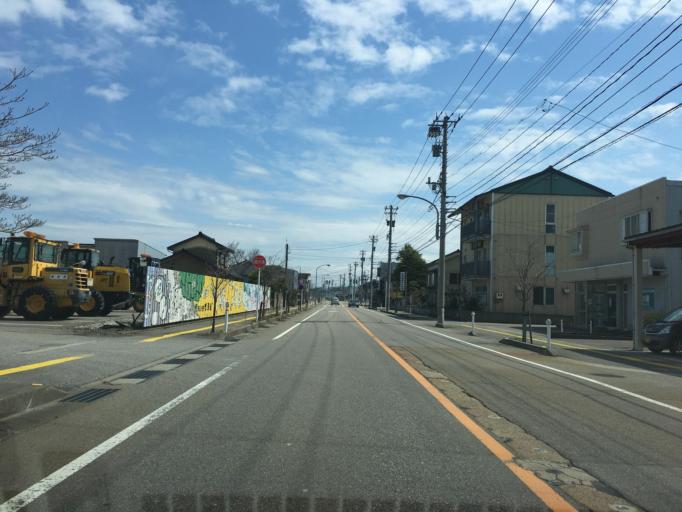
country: JP
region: Toyama
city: Nishishinminato
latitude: 36.7842
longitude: 137.0723
